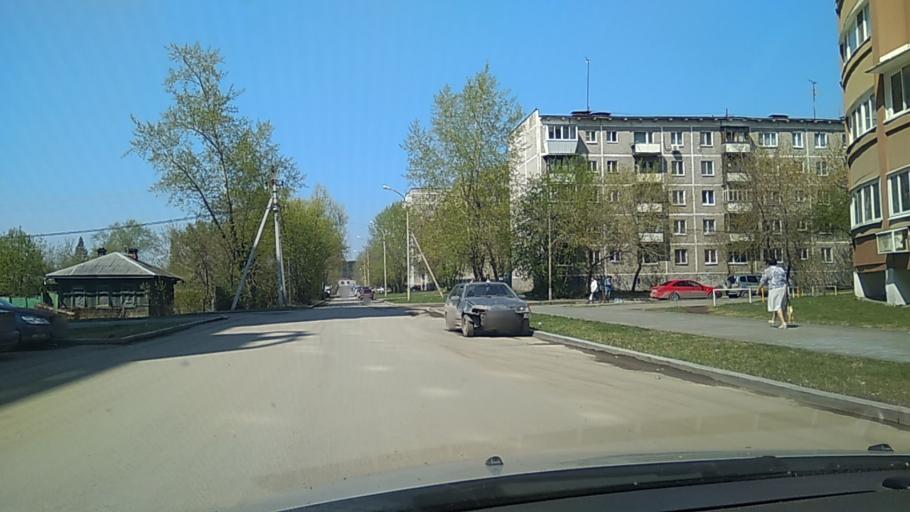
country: RU
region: Sverdlovsk
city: Yekaterinburg
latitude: 56.9087
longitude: 60.5878
